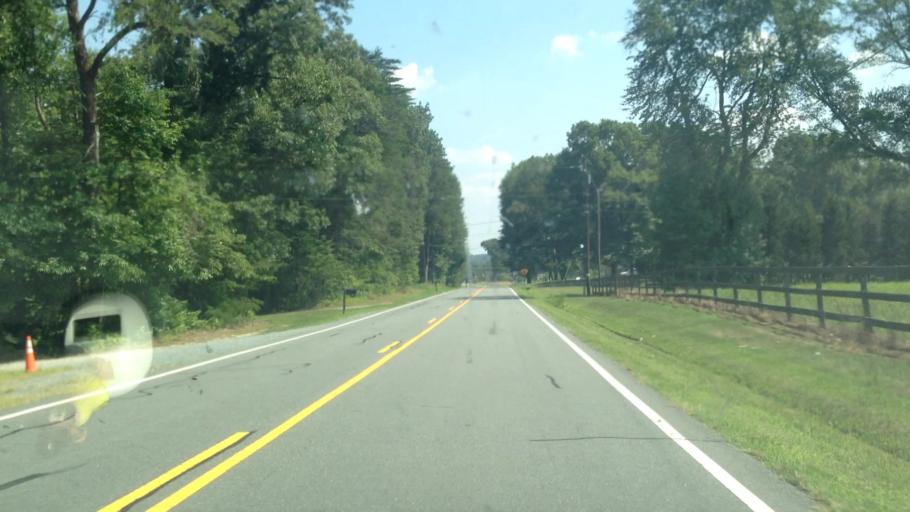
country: US
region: North Carolina
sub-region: Stokes County
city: Walnut Cove
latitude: 36.3442
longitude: -80.0528
